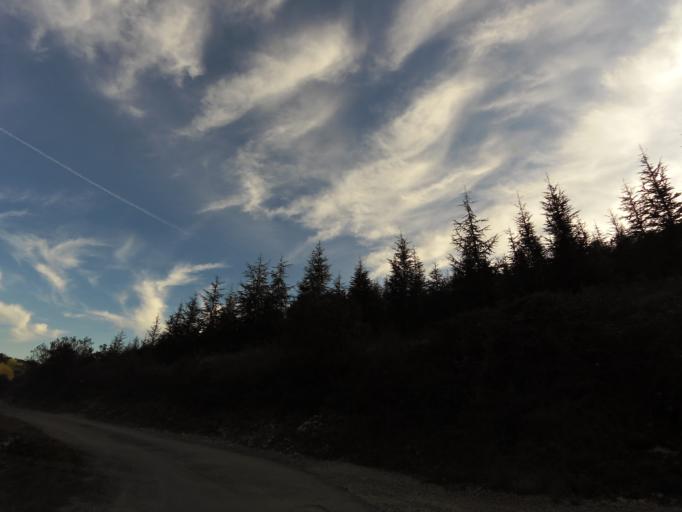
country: FR
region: Languedoc-Roussillon
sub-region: Departement du Gard
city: Congenies
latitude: 43.7877
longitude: 4.1663
